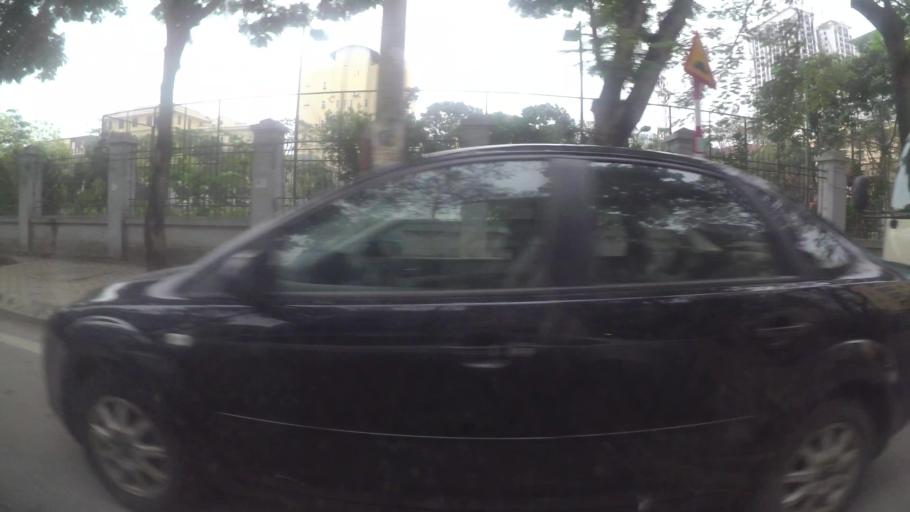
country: VN
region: Ha Noi
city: Cau Dien
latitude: 21.0377
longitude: 105.7659
